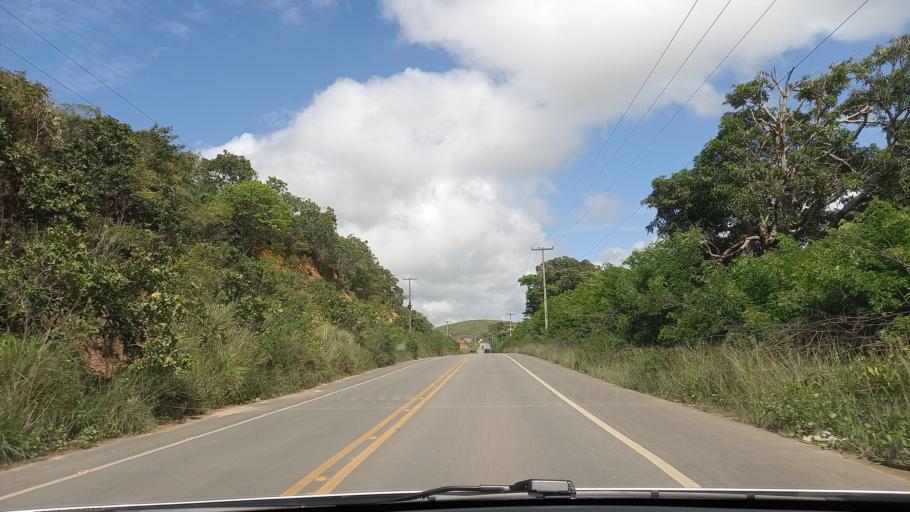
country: BR
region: Alagoas
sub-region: Maragogi
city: Maragogi
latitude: -8.9973
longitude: -35.2145
